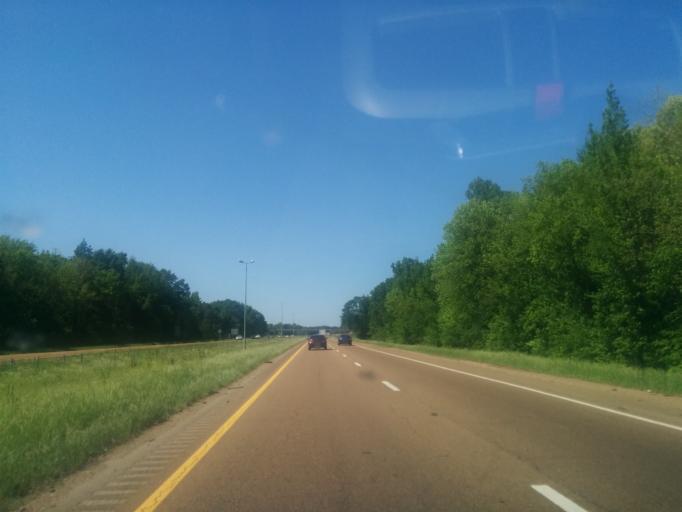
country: US
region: Mississippi
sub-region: Hinds County
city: Jackson
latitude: 32.3145
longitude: -90.2467
